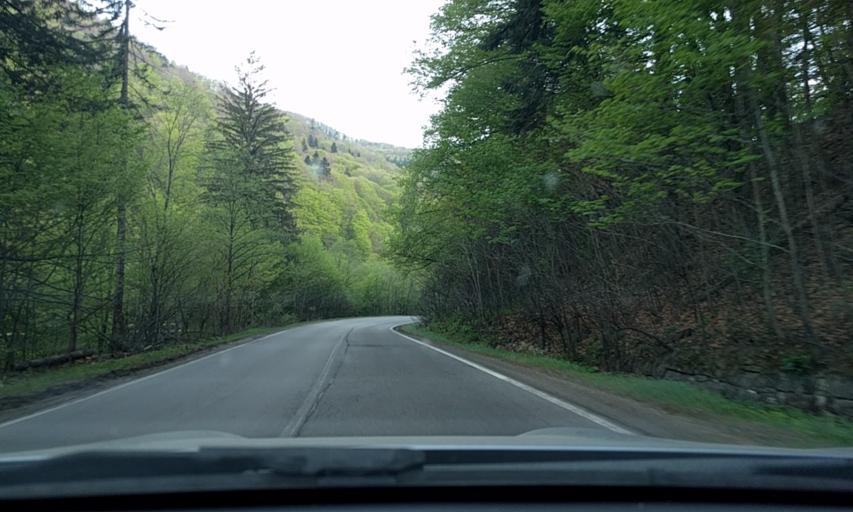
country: RO
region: Covasna
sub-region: Comuna Bretcu
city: Bretcu
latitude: 46.1069
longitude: 26.4119
